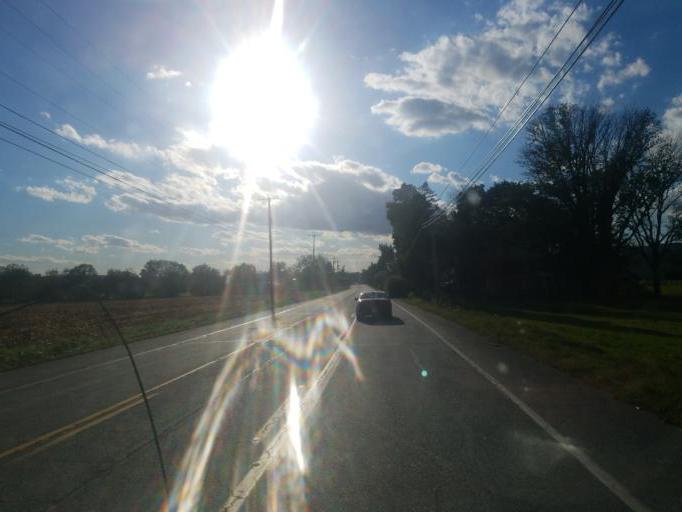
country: US
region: Pennsylvania
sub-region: York County
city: Wrightsville
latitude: 40.0183
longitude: -76.5641
